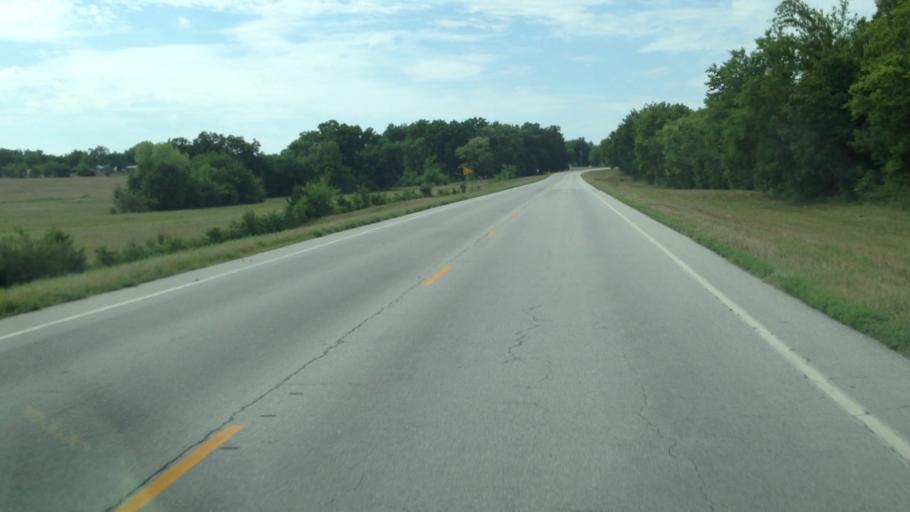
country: US
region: Kansas
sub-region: Labette County
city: Oswego
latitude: 37.1511
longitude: -95.1060
